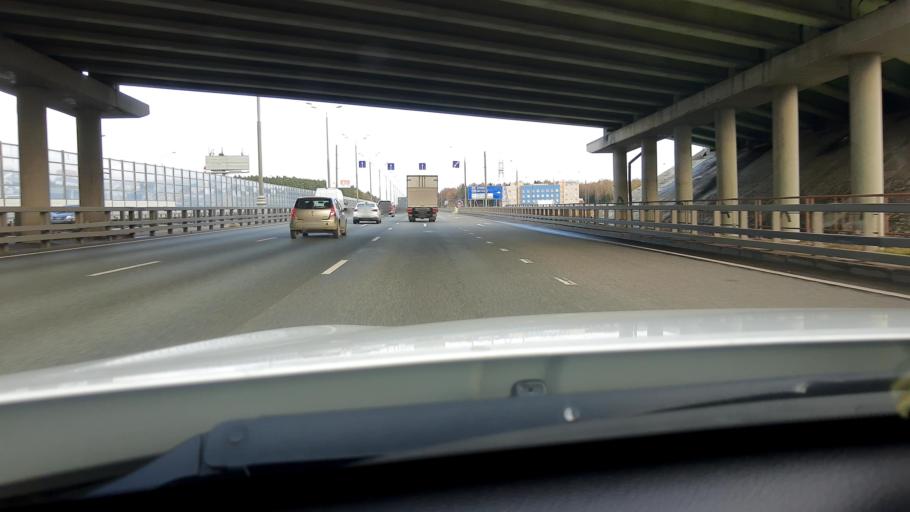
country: RU
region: Moskovskaya
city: Aprelevka
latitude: 55.5387
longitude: 37.0802
